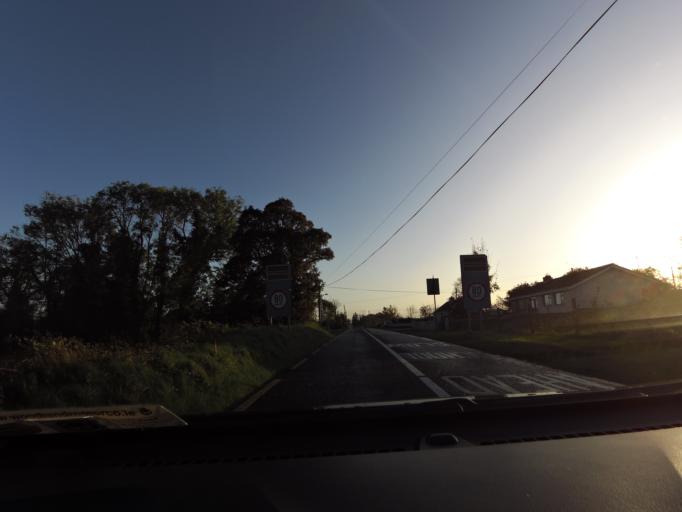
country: IE
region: Connaught
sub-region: Roscommon
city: Castlerea
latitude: 53.7310
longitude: -8.5539
